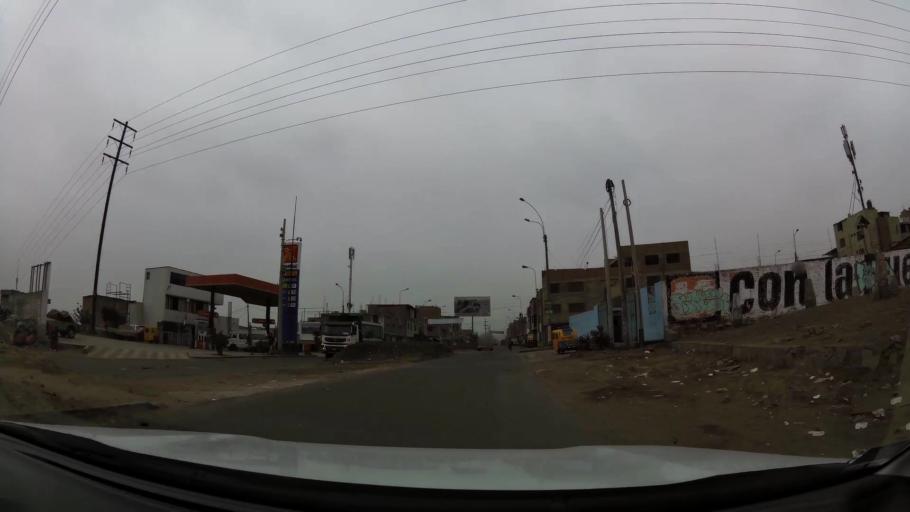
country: PE
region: Lima
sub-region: Lima
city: Surco
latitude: -12.1797
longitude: -76.9626
